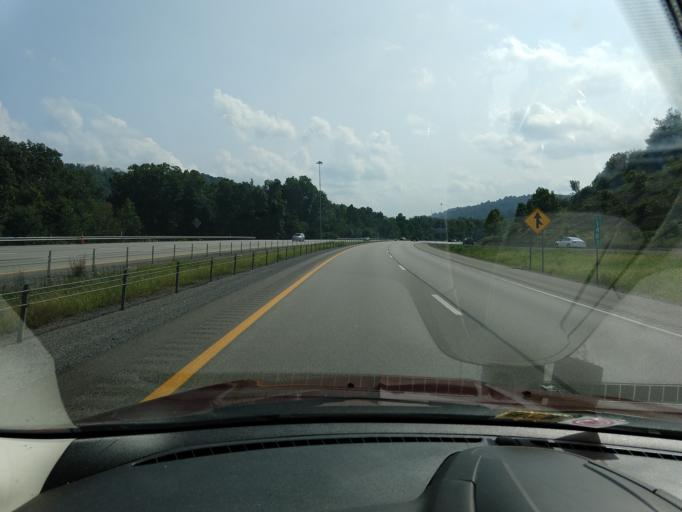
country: US
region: West Virginia
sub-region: Monongalia County
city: Morgantown
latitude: 39.5694
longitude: -79.9805
